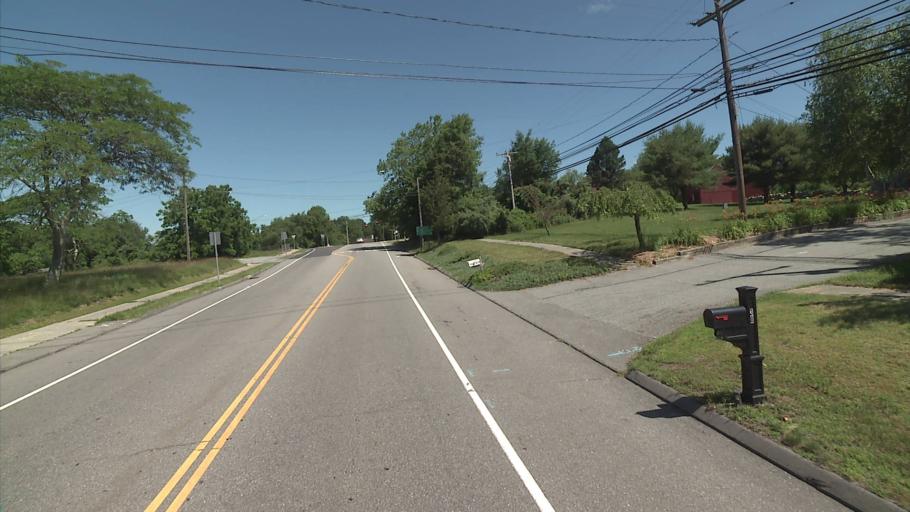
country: US
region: Connecticut
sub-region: New London County
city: Poquonock Bridge
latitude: 41.3440
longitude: -72.0112
